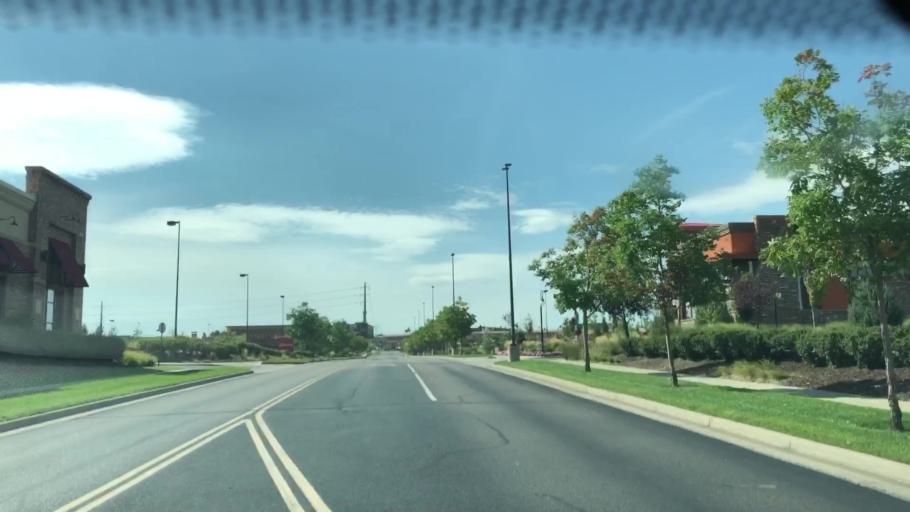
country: US
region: Colorado
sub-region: Douglas County
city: Parker
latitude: 39.6028
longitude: -104.7073
